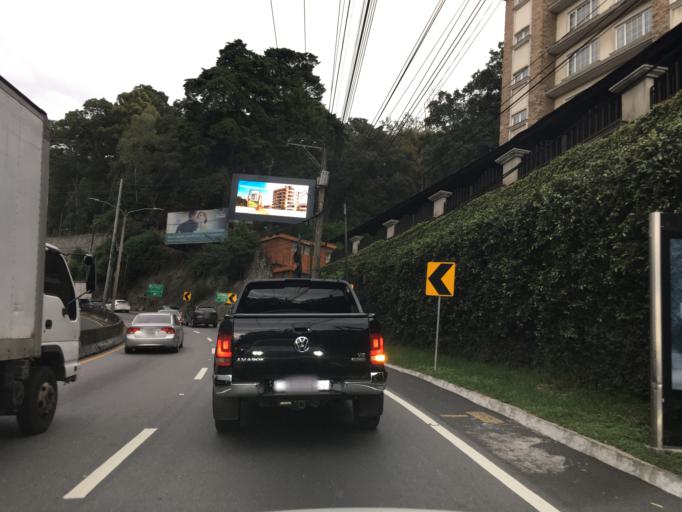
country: GT
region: Guatemala
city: Santa Catarina Pinula
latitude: 14.5710
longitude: -90.4835
